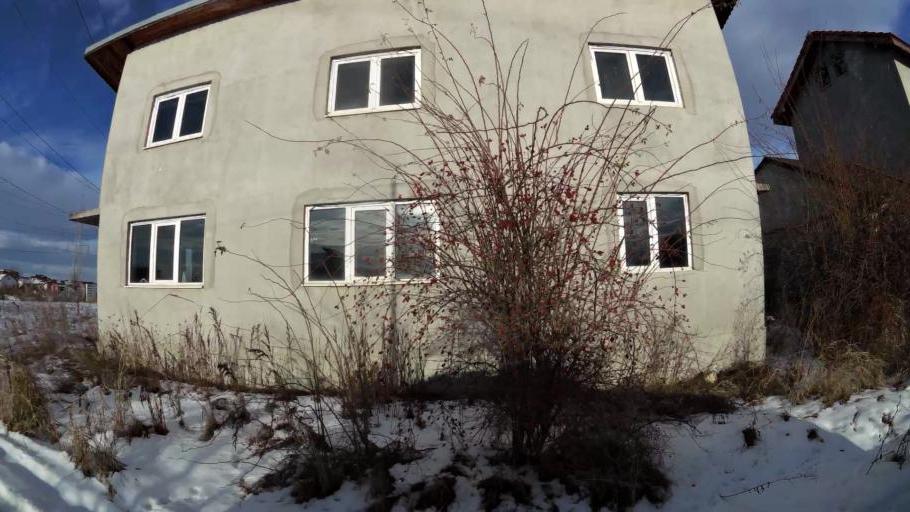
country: RO
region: Ilfov
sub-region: Comuna Fundeni-Dobroesti
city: Fundeni
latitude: 44.4614
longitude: 26.1739
